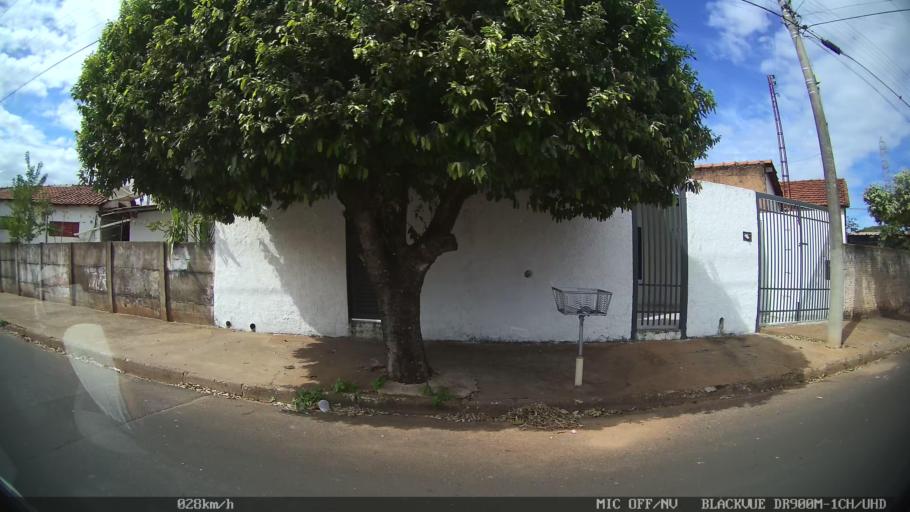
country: BR
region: Sao Paulo
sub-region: Bady Bassitt
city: Bady Bassitt
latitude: -20.8115
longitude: -49.5156
